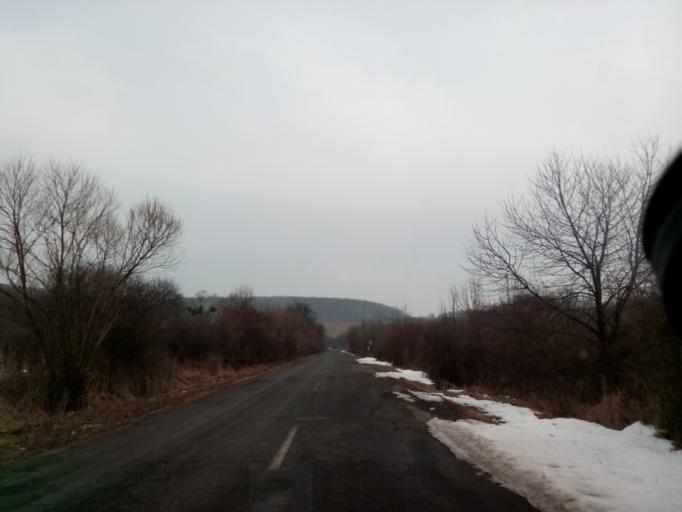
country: HU
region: Borsod-Abauj-Zemplen
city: Gonc
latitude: 48.4882
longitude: 21.3781
